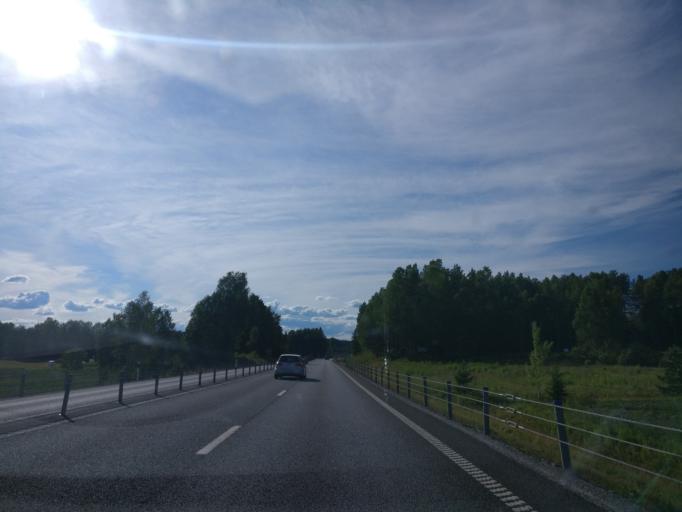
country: SE
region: Vaermland
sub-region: Arvika Kommun
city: Arvika
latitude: 59.6536
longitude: 12.6602
